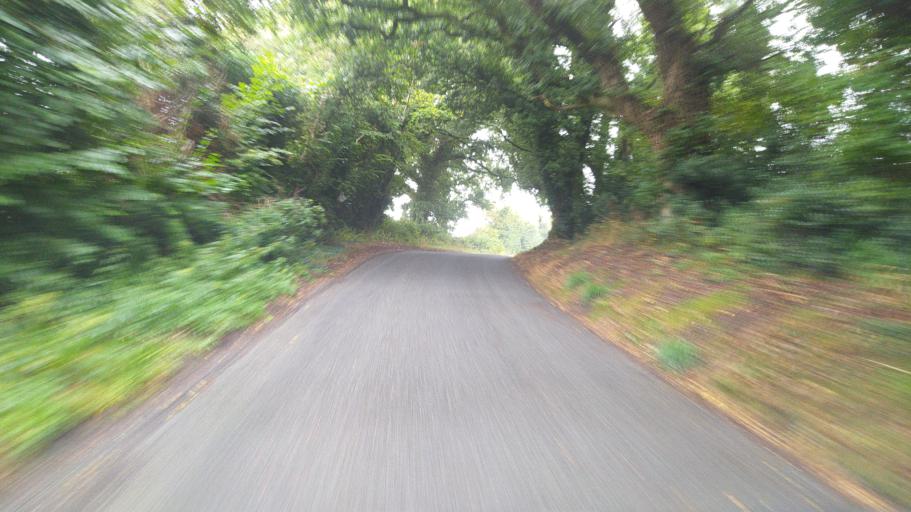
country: GB
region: England
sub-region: Wiltshire
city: Ansty
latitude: 50.9983
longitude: -2.1183
